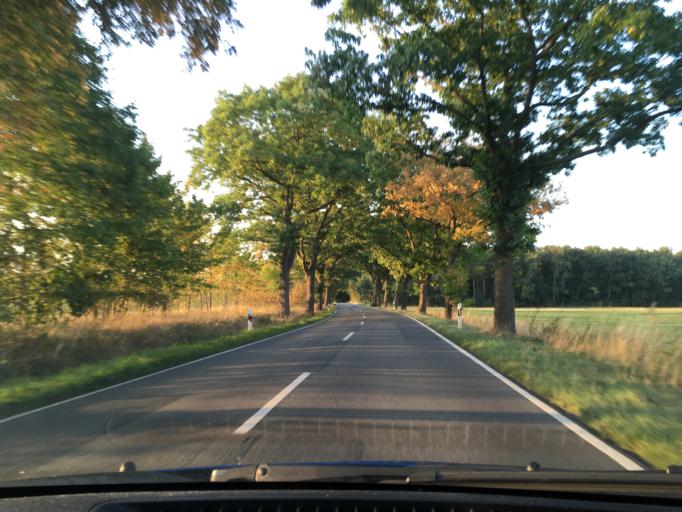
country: DE
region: Lower Saxony
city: Bleckede
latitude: 53.2646
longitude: 10.7437
